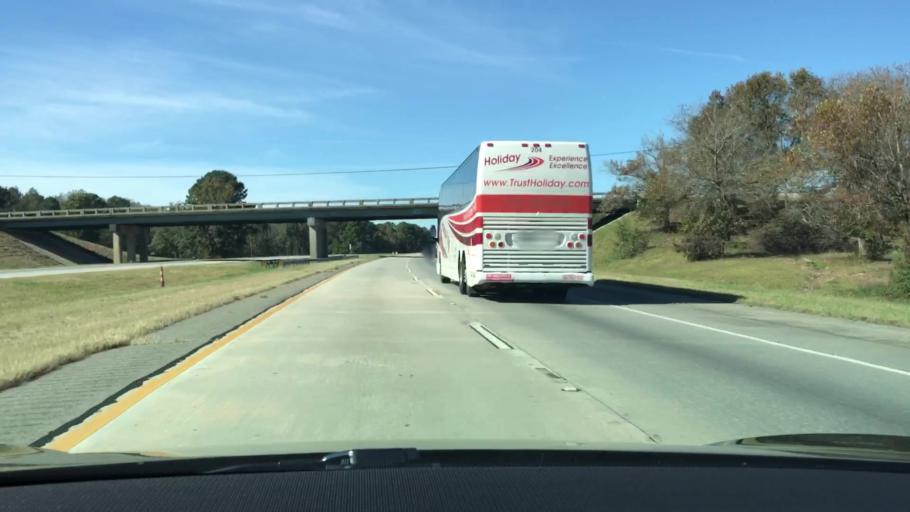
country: US
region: Georgia
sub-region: Greene County
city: Union Point
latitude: 33.5442
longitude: -83.0786
